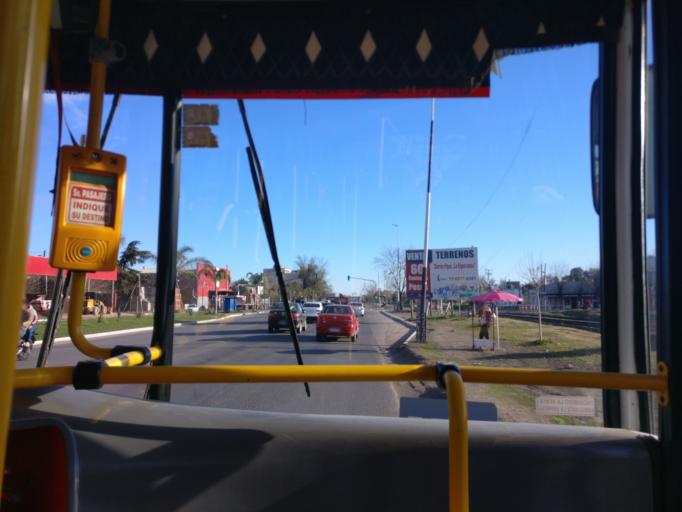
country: AR
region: Buenos Aires
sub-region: Partido de Ezeiza
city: Ezeiza
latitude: -34.8793
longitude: -58.5547
